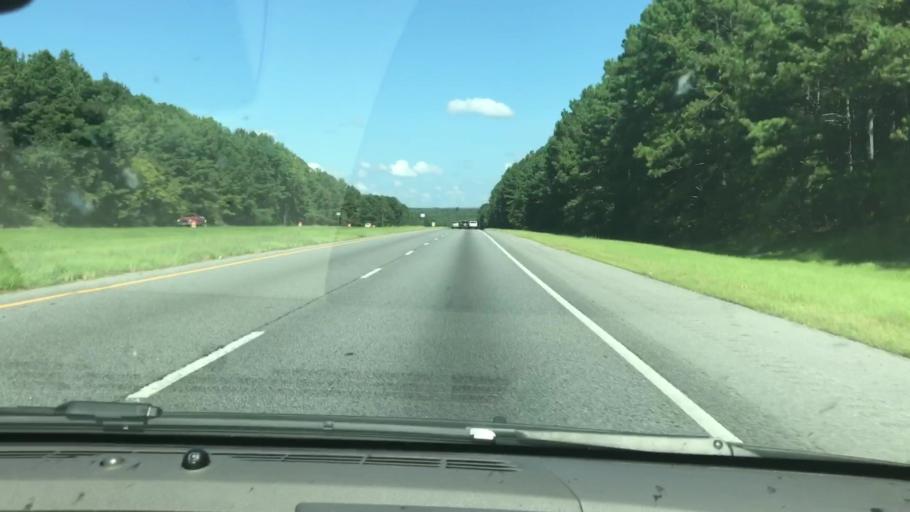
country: US
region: Georgia
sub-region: Harris County
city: Hamilton
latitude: 32.6275
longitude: -84.9582
